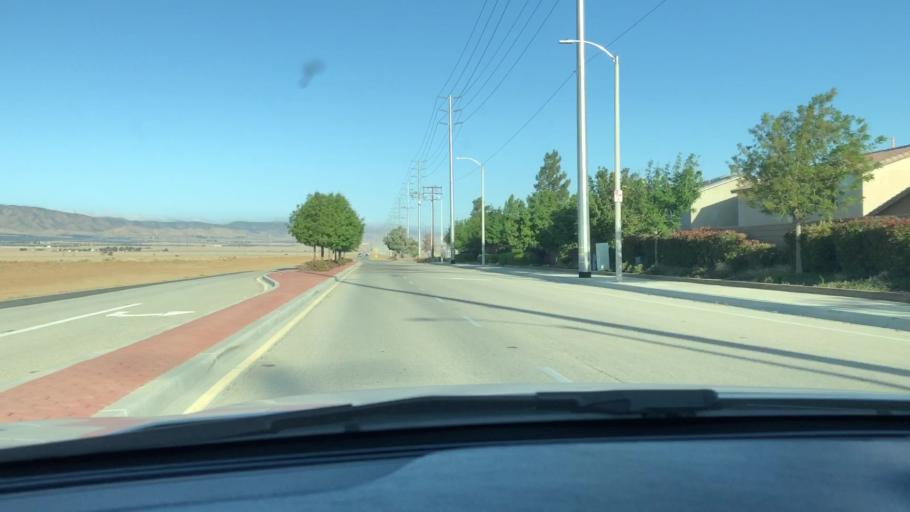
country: US
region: California
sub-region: Los Angeles County
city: Quartz Hill
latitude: 34.6748
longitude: -118.2413
